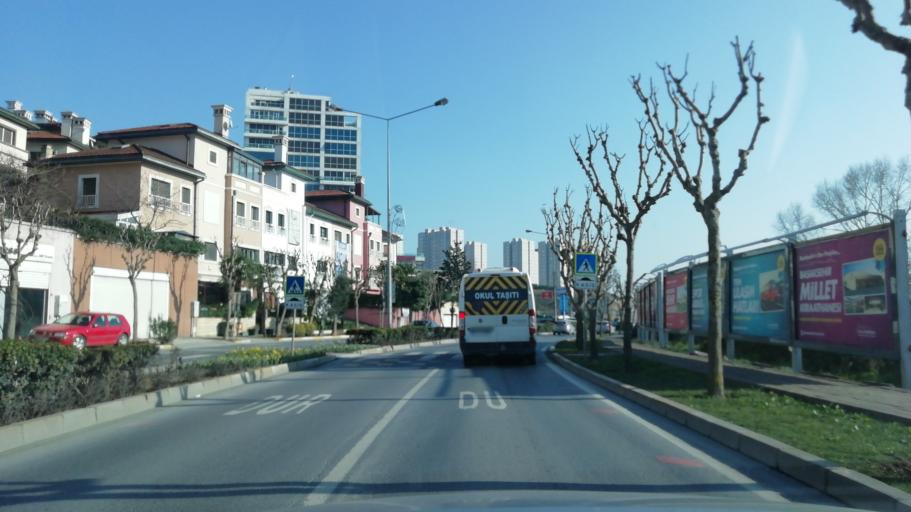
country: TR
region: Istanbul
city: Esenyurt
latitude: 41.0656
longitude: 28.6984
